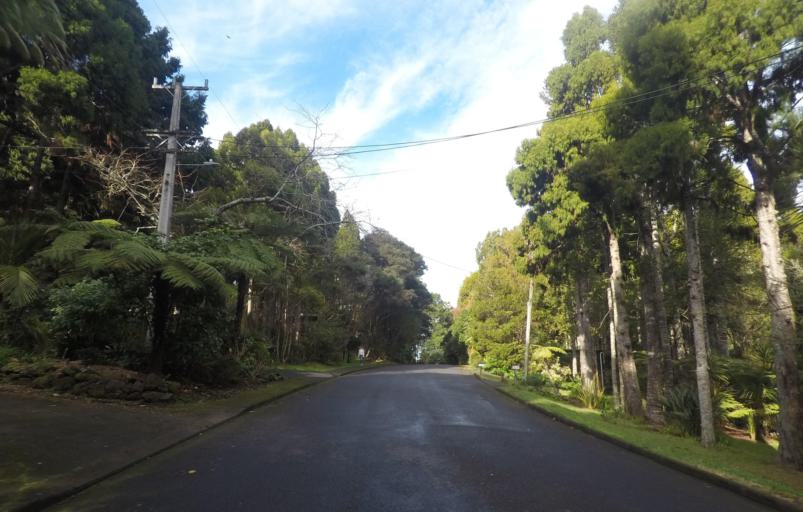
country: NZ
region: Auckland
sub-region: Auckland
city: Titirangi
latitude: -36.9410
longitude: 174.6416
